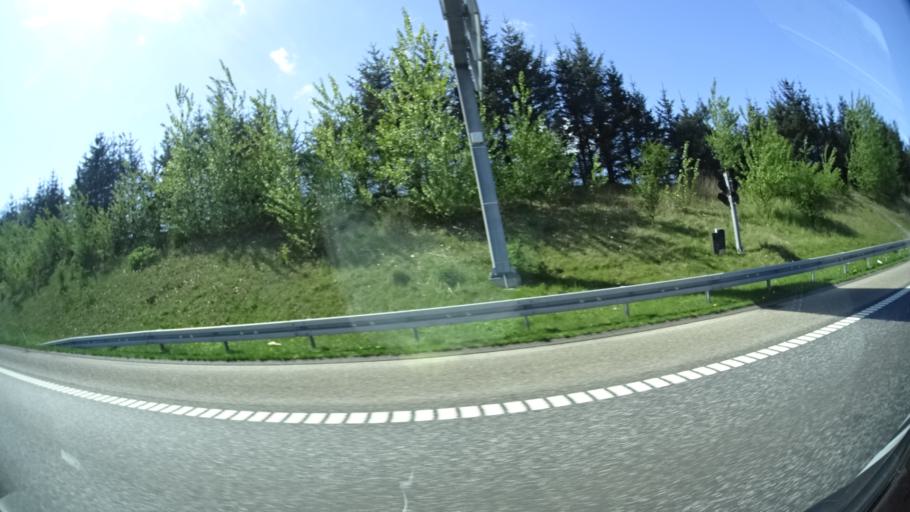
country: DK
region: Central Jutland
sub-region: Arhus Kommune
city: Trige
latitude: 56.2350
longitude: 10.1250
